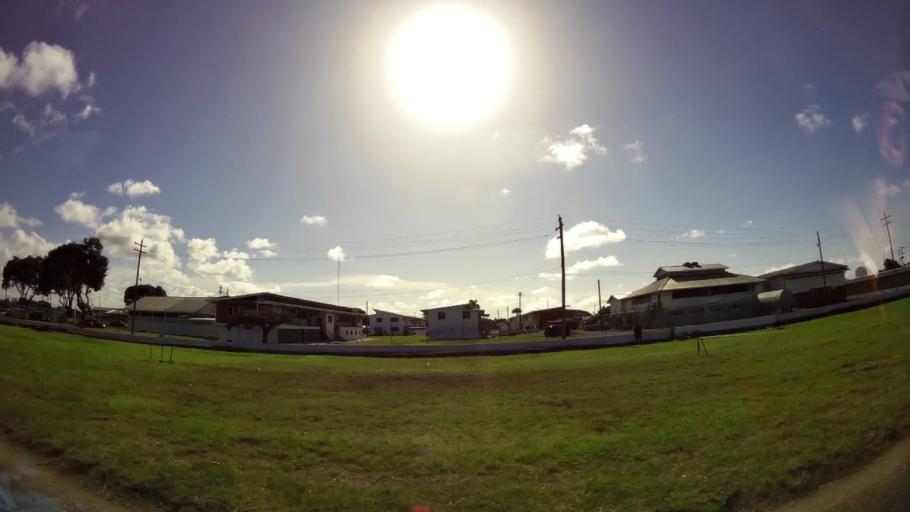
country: GY
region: Demerara-Mahaica
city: Georgetown
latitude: 6.8197
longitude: -58.1449
